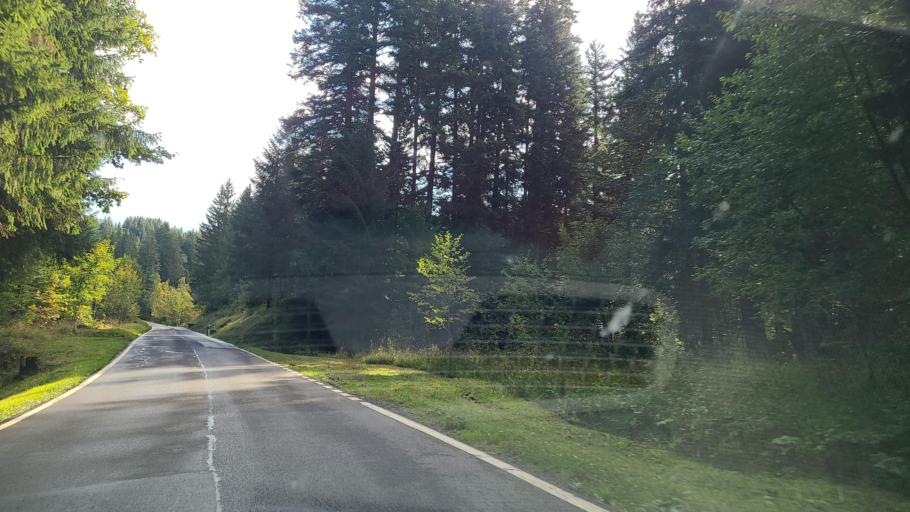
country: CH
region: Schwyz
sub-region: Bezirk March
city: Altendorf
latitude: 47.1281
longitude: 8.8347
